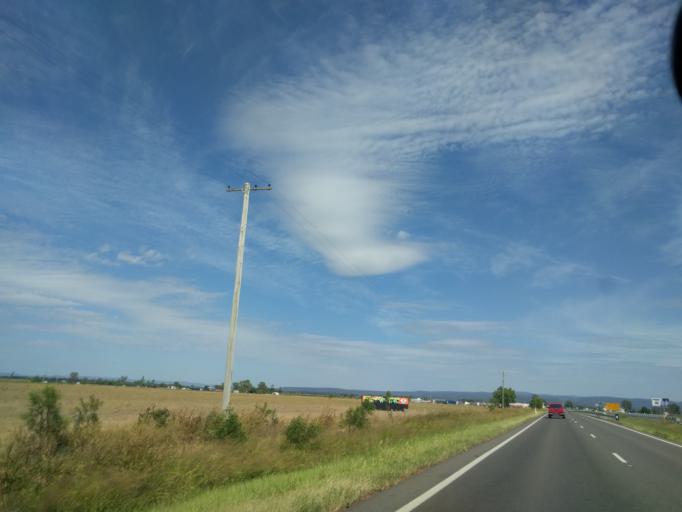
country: AU
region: Queensland
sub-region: Lockyer Valley
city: Gatton
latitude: -27.5489
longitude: 152.3844
